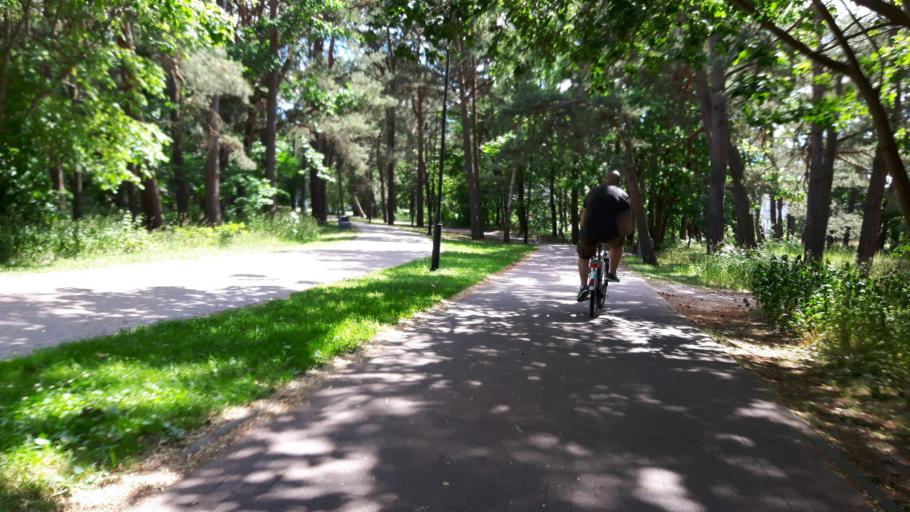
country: PL
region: Pomeranian Voivodeship
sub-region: Sopot
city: Sopot
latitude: 54.4267
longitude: 18.5939
